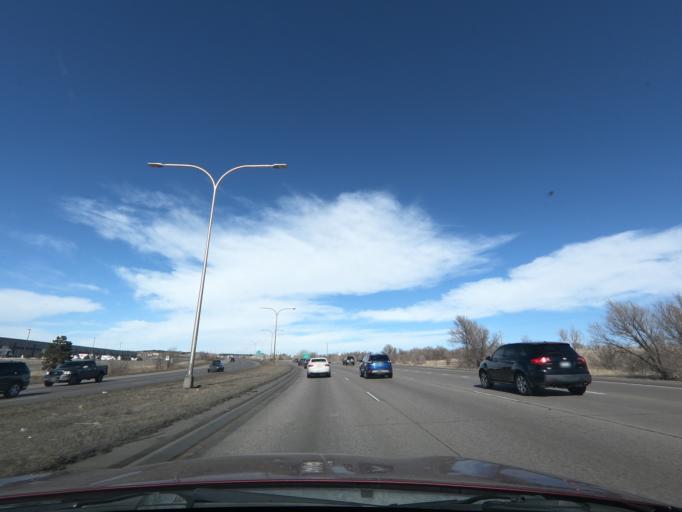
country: US
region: Colorado
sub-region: El Paso County
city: Cimarron Hills
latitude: 38.8313
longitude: -104.7205
